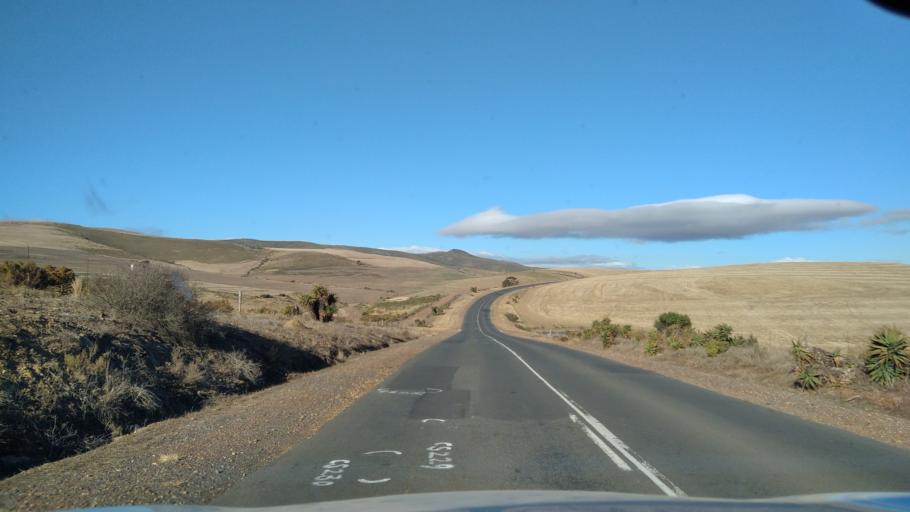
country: ZA
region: Western Cape
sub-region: Overberg District Municipality
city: Caledon
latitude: -34.1687
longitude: 19.2903
